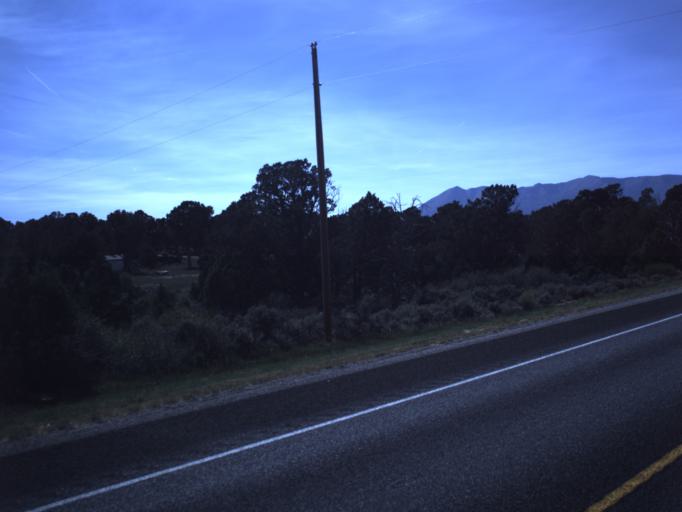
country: US
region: Utah
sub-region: San Juan County
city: Monticello
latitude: 37.8595
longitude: -109.2054
